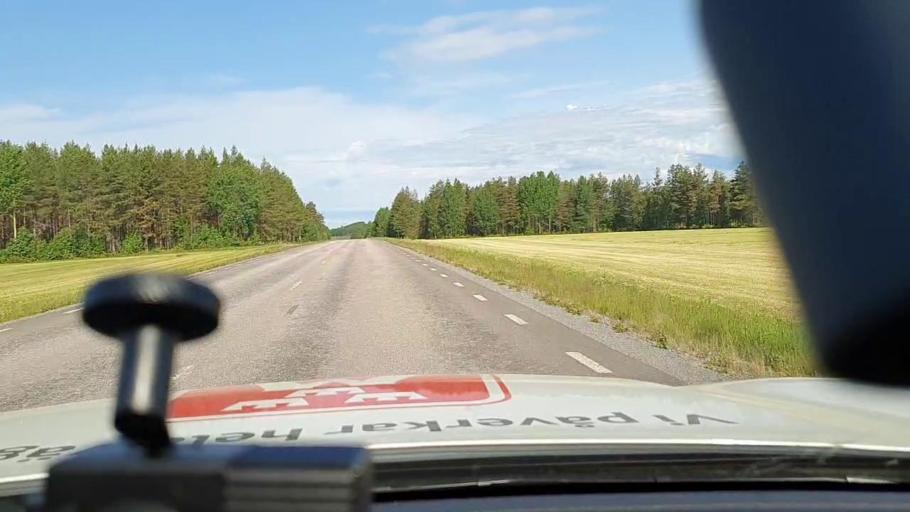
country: SE
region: Norrbotten
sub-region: Bodens Kommun
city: Boden
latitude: 65.9057
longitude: 21.3623
